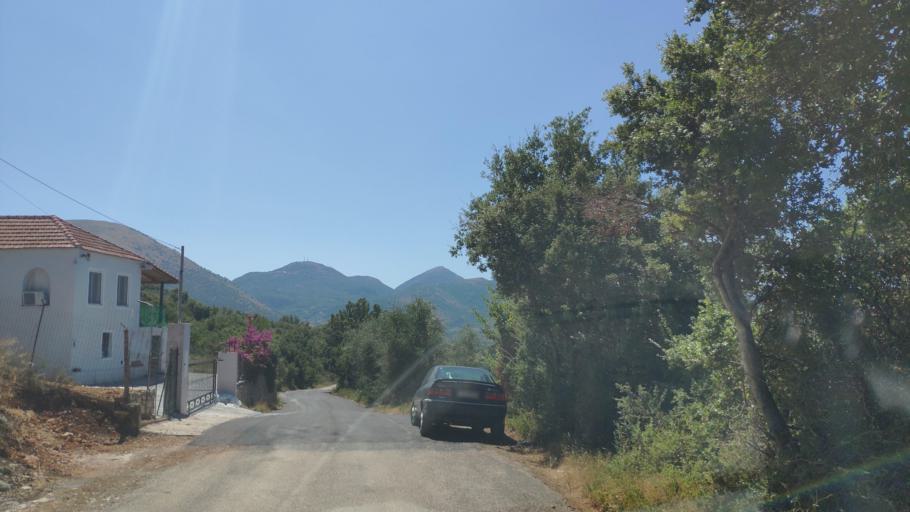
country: GR
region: Epirus
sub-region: Nomos Prevezis
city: Kanalaki
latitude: 39.2735
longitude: 20.5996
